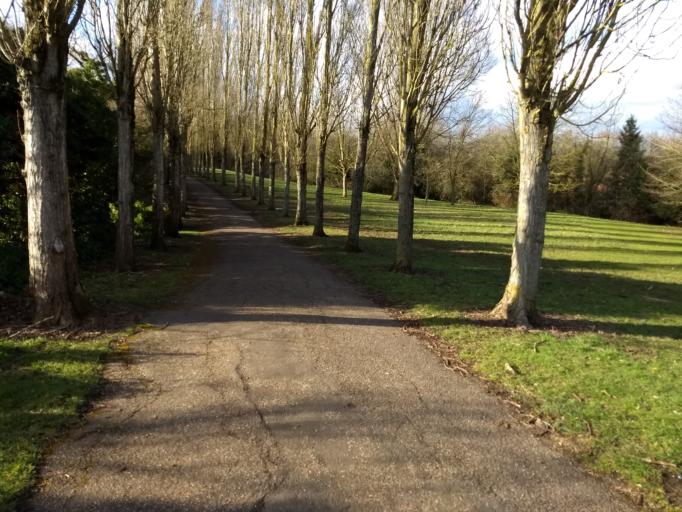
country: GB
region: England
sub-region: Milton Keynes
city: Milton Keynes
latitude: 52.0441
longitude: -0.7306
